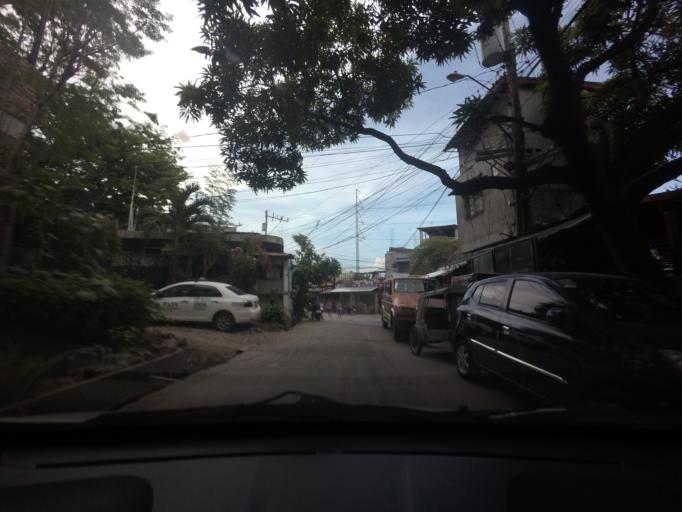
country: PH
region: Calabarzon
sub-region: Province of Rizal
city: Taguig
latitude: 14.5234
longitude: 121.0604
